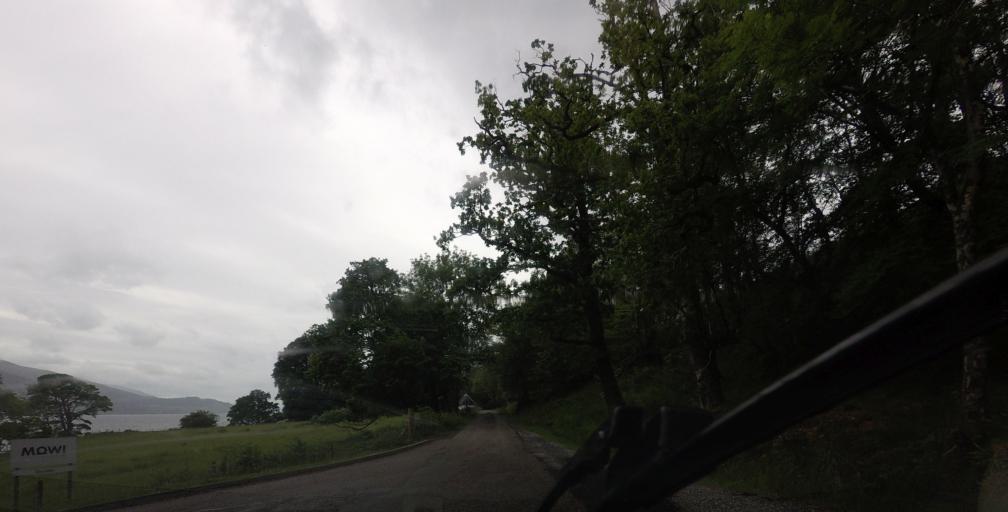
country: GB
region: Scotland
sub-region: Highland
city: Fort William
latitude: 56.7885
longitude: -5.1806
